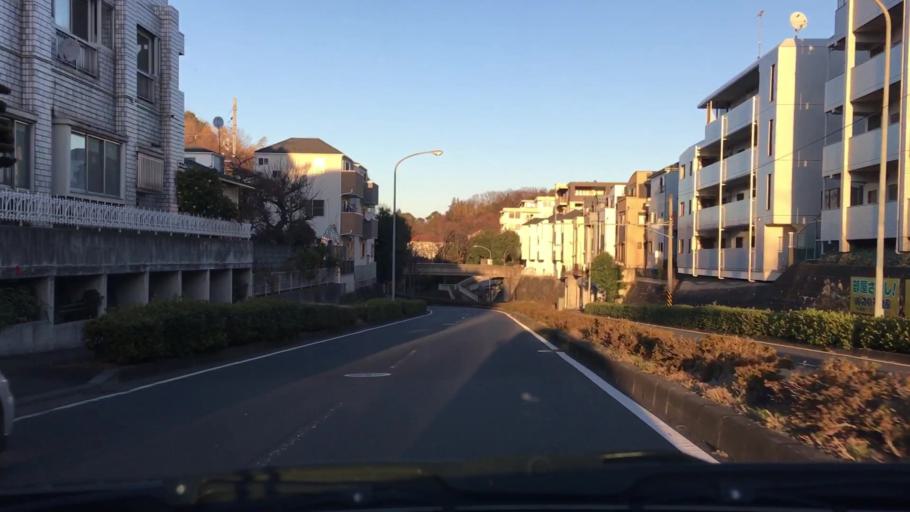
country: JP
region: Tokyo
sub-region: Machida-shi
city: Machida
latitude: 35.5485
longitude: 139.5583
